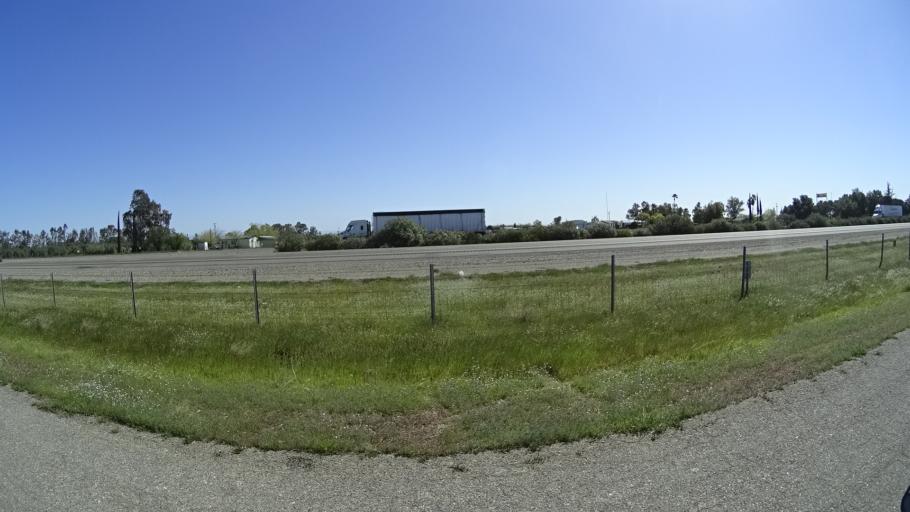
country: US
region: California
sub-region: Glenn County
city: Orland
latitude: 39.7017
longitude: -122.2064
